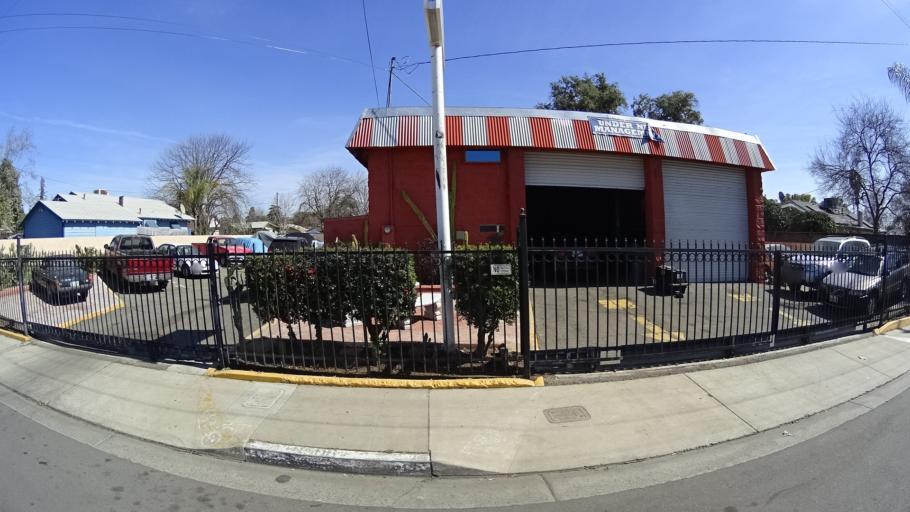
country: US
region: California
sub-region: Fresno County
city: Fresno
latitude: 36.7631
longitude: -119.8086
